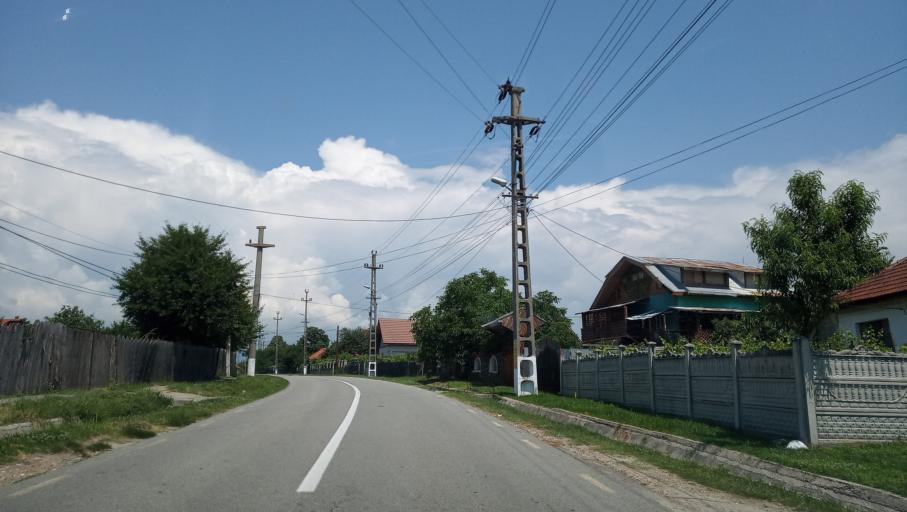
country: RO
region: Gorj
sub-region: Comuna Turcinesti
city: Turcinesti
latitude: 45.0638
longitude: 23.3482
